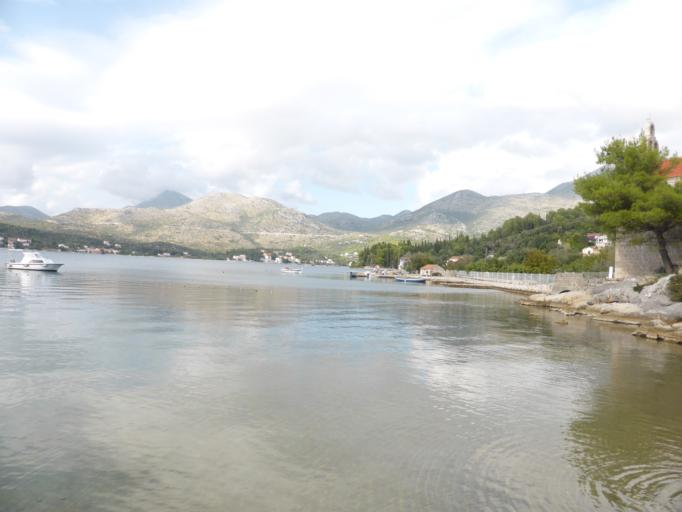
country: HR
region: Dubrovacko-Neretvanska
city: Podgora
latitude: 42.7733
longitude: 17.8836
